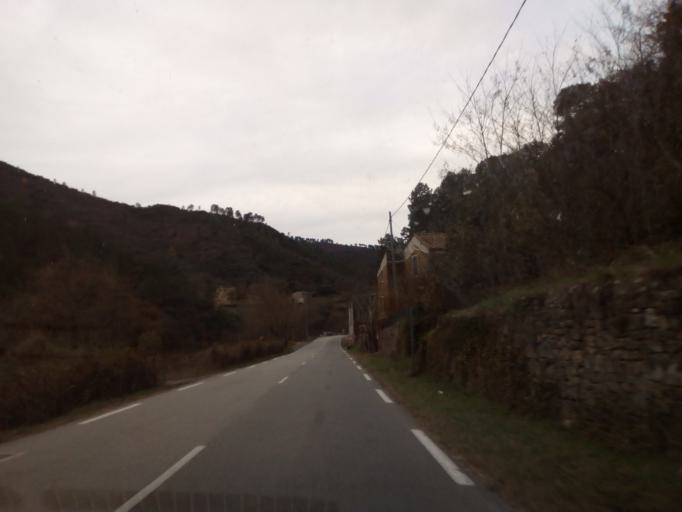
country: FR
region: Languedoc-Roussillon
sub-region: Departement du Gard
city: Saint-Jean-du-Gard
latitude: 44.1137
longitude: 3.8658
